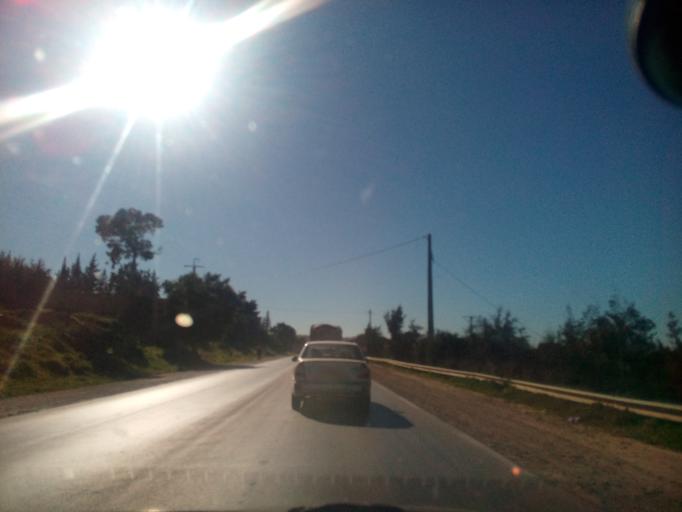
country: DZ
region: Relizane
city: Djidiouia
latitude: 35.9343
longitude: 0.8503
